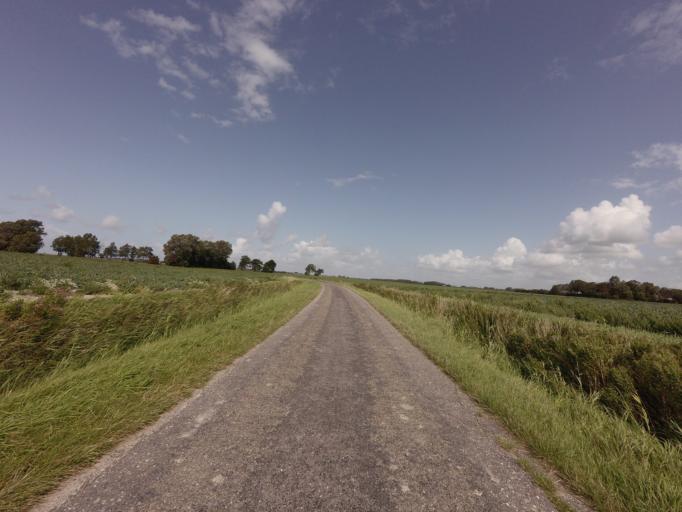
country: NL
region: Friesland
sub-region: Gemeente Harlingen
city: Harlingen
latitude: 53.1212
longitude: 5.4418
